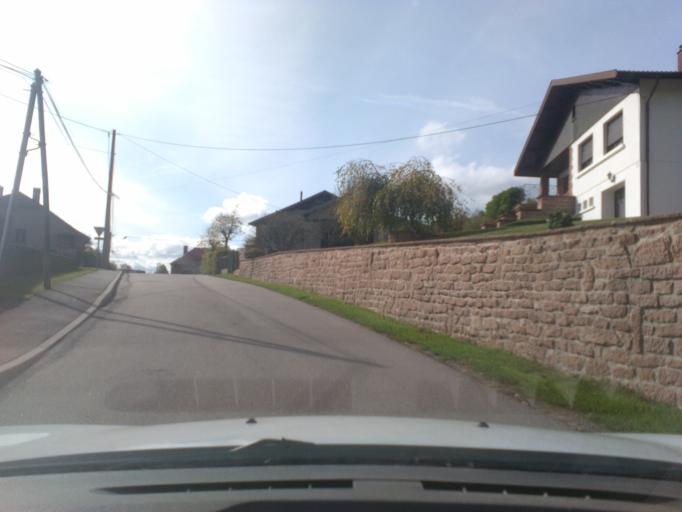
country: FR
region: Lorraine
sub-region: Departement des Vosges
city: Sainte-Marguerite
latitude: 48.2980
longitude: 7.0076
